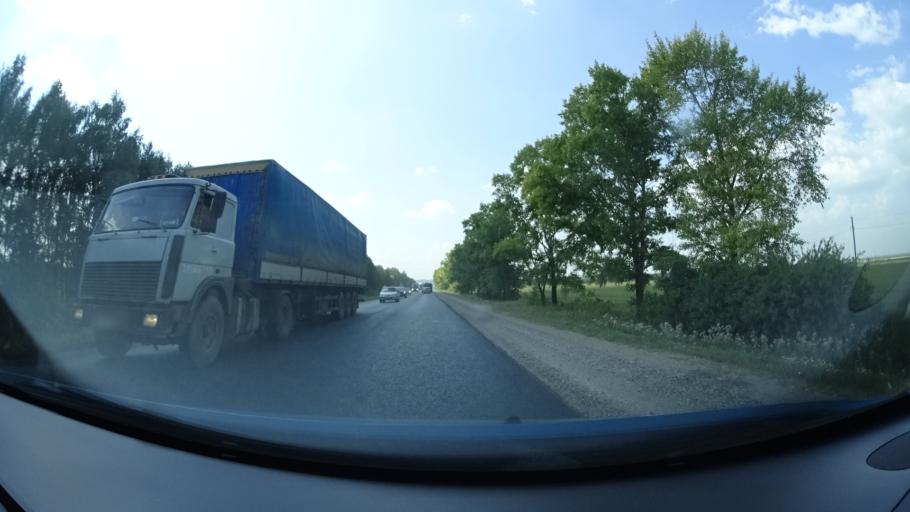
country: RU
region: Bashkortostan
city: Kandry
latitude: 54.5271
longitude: 54.0650
